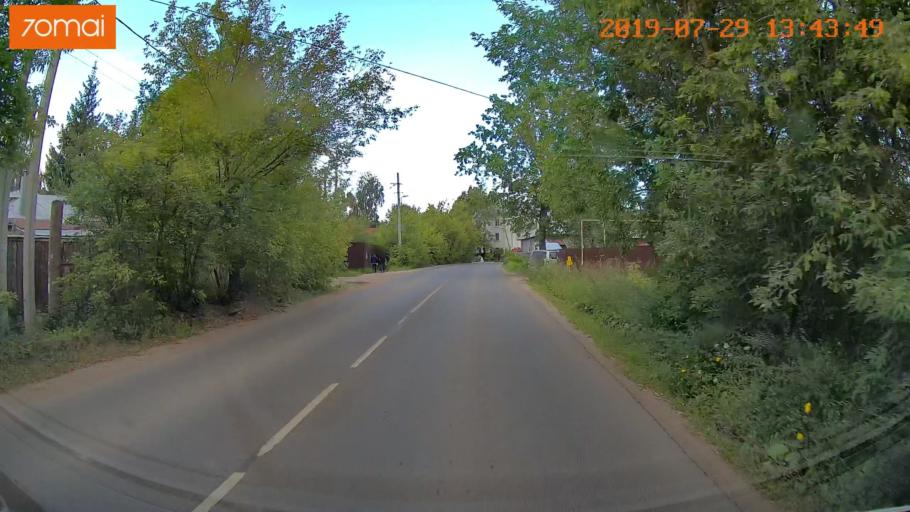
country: RU
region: Ivanovo
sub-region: Gorod Ivanovo
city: Ivanovo
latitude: 57.0069
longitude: 40.9298
